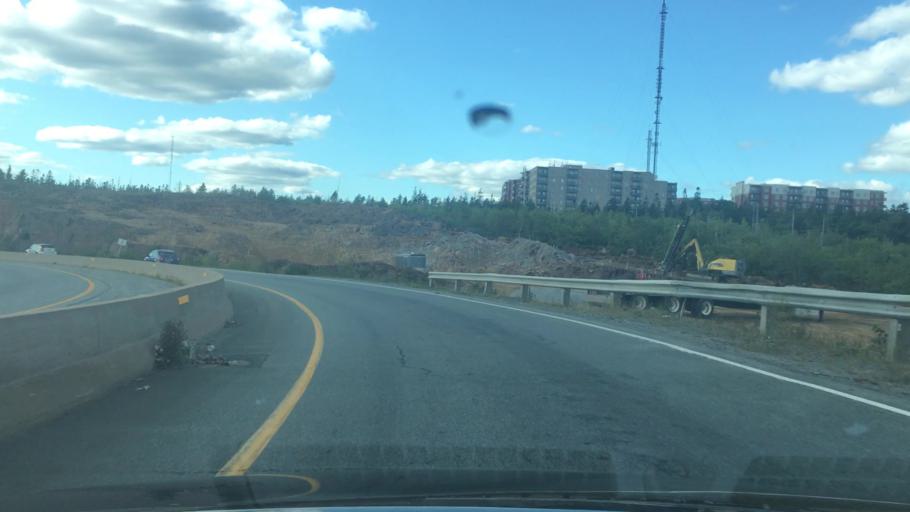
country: CA
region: Nova Scotia
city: Dartmouth
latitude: 44.6450
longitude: -63.6550
